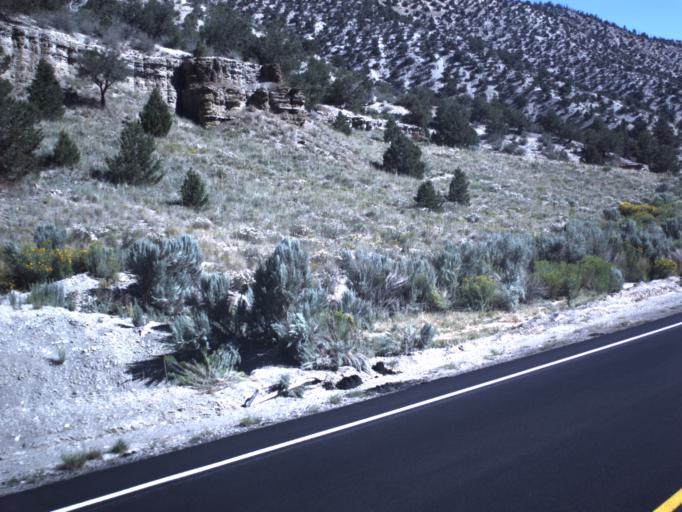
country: US
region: Utah
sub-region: Carbon County
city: Helper
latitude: 39.9488
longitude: -110.6565
